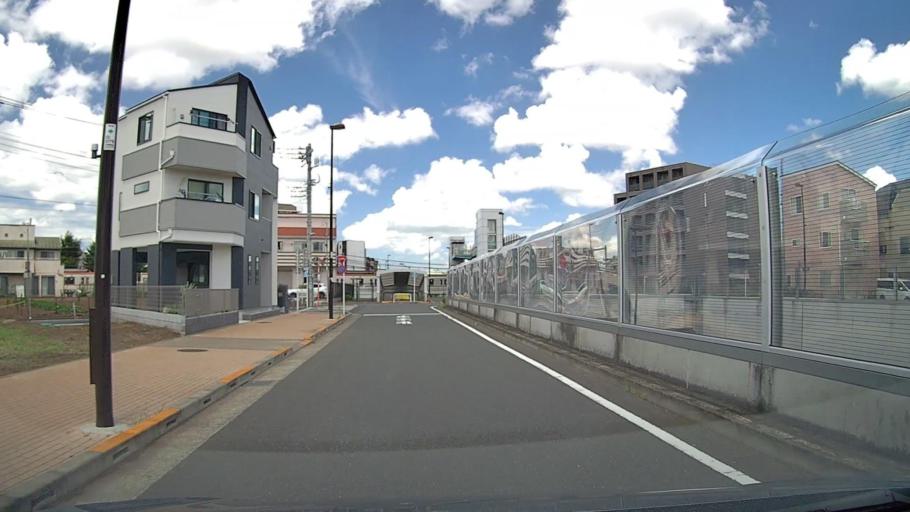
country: JP
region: Tokyo
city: Nishi-Tokyo-shi
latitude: 35.7464
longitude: 139.5582
